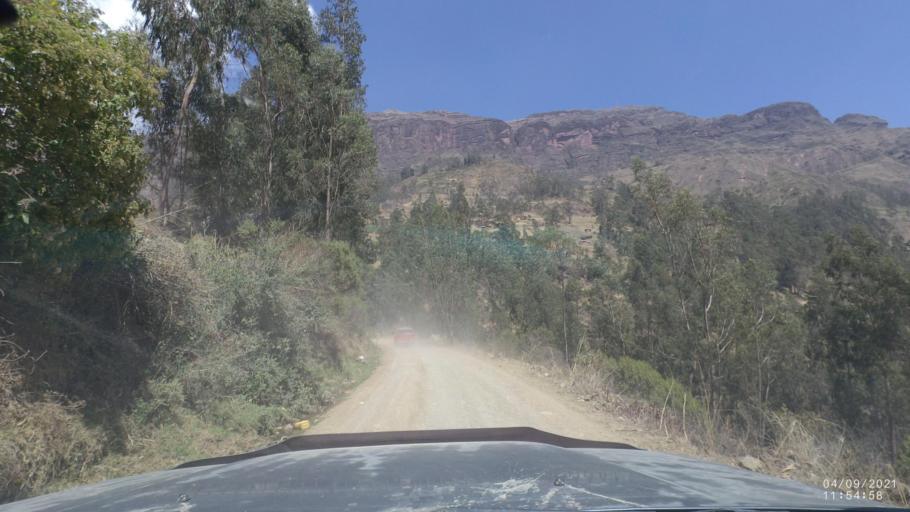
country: BO
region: Cochabamba
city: Colchani
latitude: -17.2395
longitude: -66.5254
